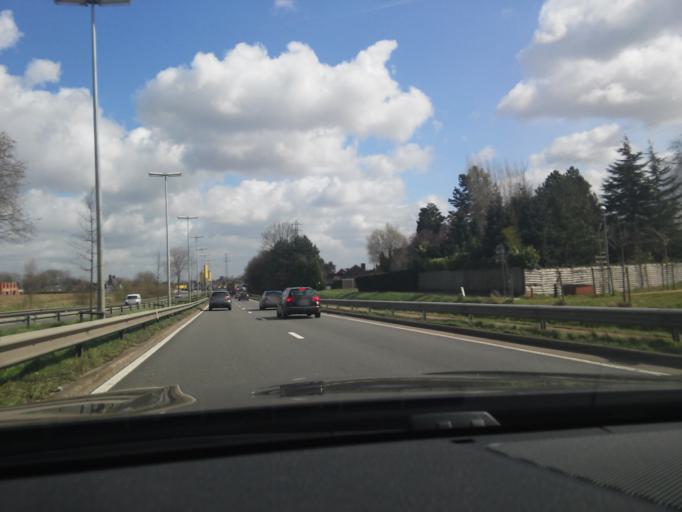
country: BE
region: Flanders
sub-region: Provincie Oost-Vlaanderen
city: Temse
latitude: 51.1341
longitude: 4.2056
